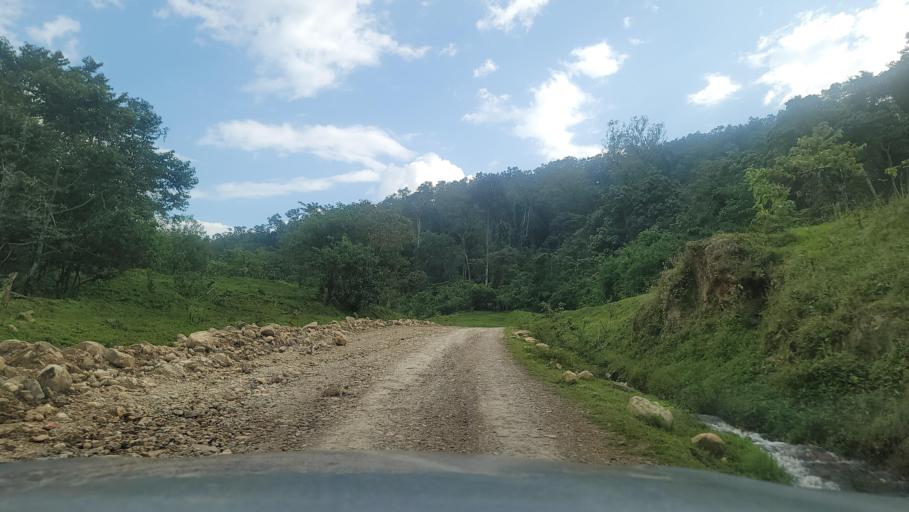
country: ET
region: Southern Nations, Nationalities, and People's Region
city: Bonga
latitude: 7.6024
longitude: 36.2022
